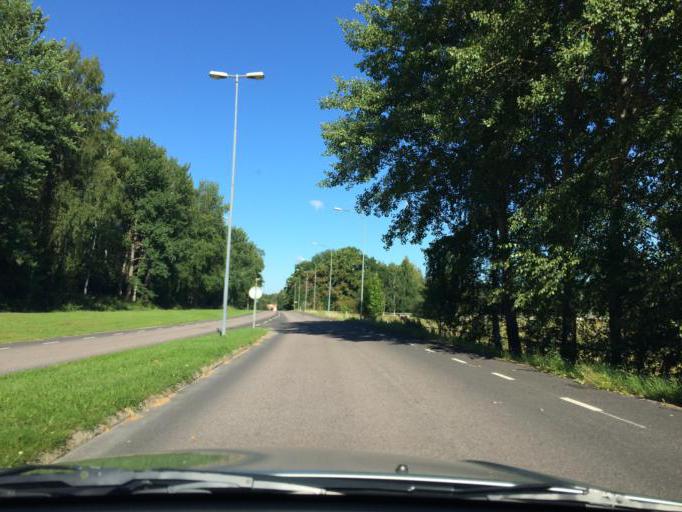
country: SE
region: Vaestmanland
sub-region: Vasteras
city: Vasteras
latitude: 59.5886
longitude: 16.6122
